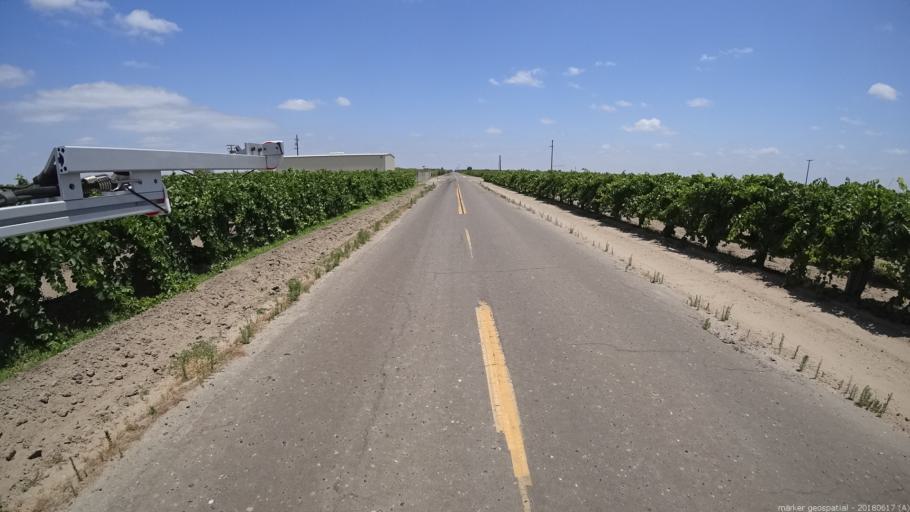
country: US
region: California
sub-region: Fresno County
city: Biola
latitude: 36.8295
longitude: -120.1069
